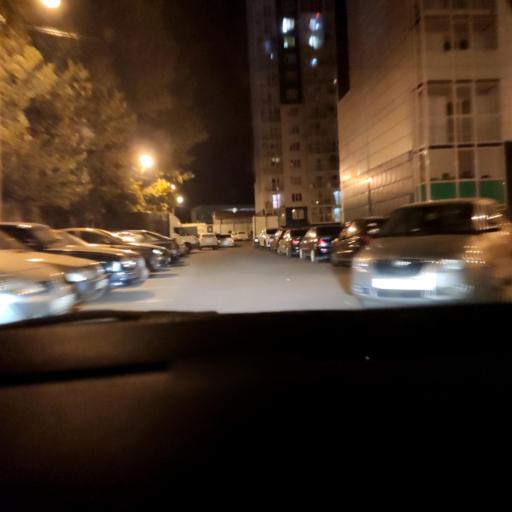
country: RU
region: Voronezj
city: Podgornoye
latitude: 51.6947
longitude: 39.1388
